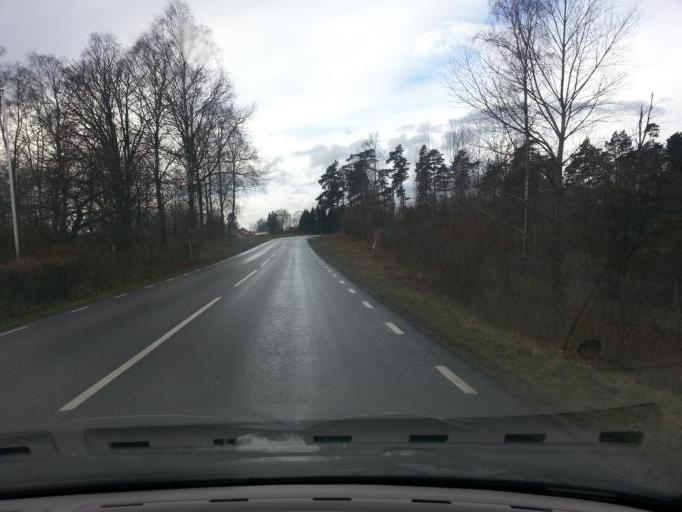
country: SE
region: Skane
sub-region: Klippans Kommun
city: Ljungbyhed
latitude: 56.0694
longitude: 13.2208
